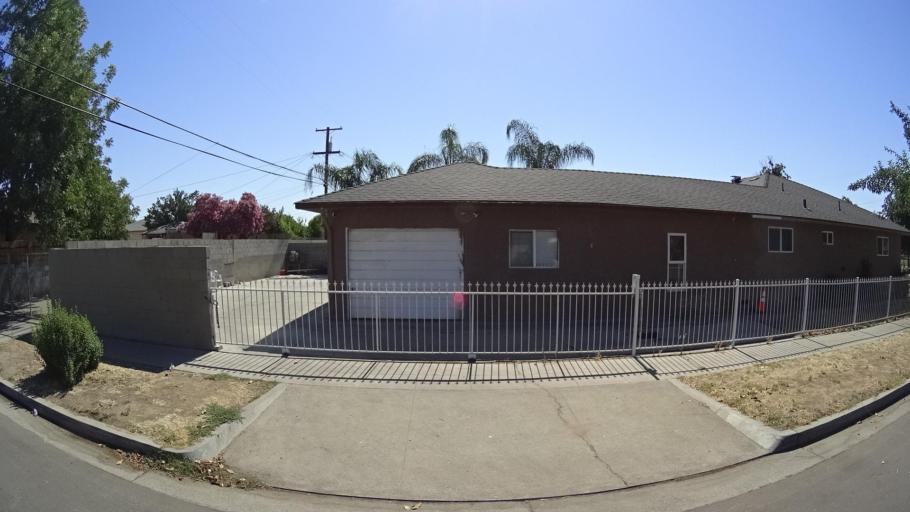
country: US
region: California
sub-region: Fresno County
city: Fresno
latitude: 36.7253
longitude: -119.7591
